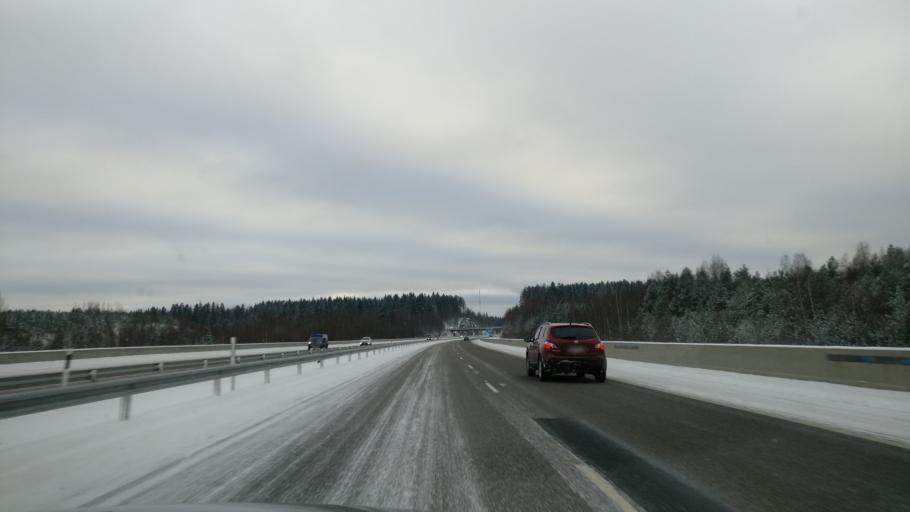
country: FI
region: Paijanne Tavastia
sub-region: Lahti
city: Nastola
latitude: 61.0082
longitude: 25.8129
